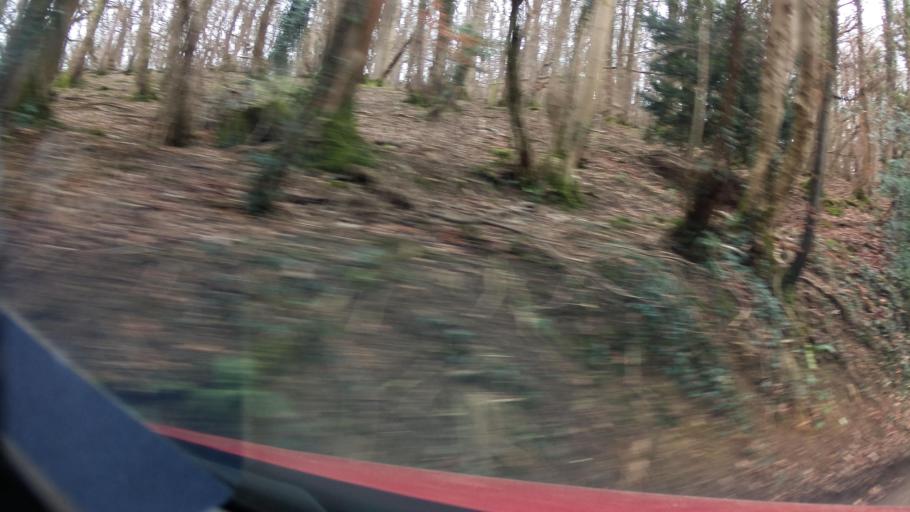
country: GB
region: England
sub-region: Wiltshire
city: Biddestone
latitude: 51.4711
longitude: -2.2301
